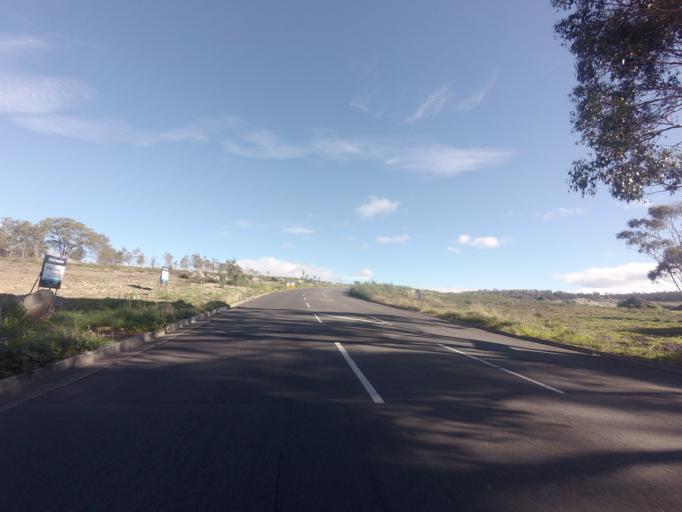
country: AU
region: Tasmania
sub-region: Clarence
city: Rokeby
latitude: -42.8868
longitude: 147.4349
